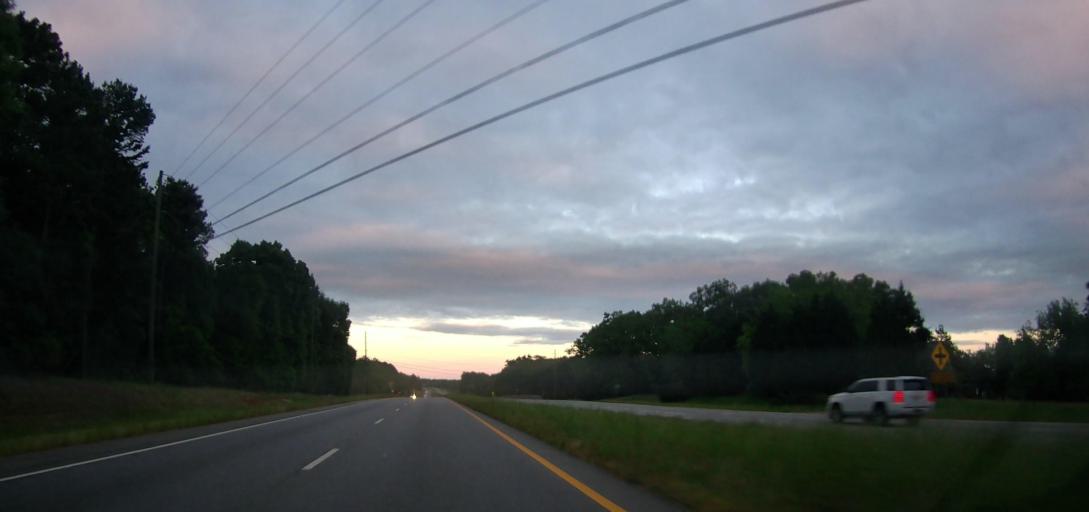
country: US
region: Georgia
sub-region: Oconee County
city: Bogart
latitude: 34.0147
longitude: -83.4888
